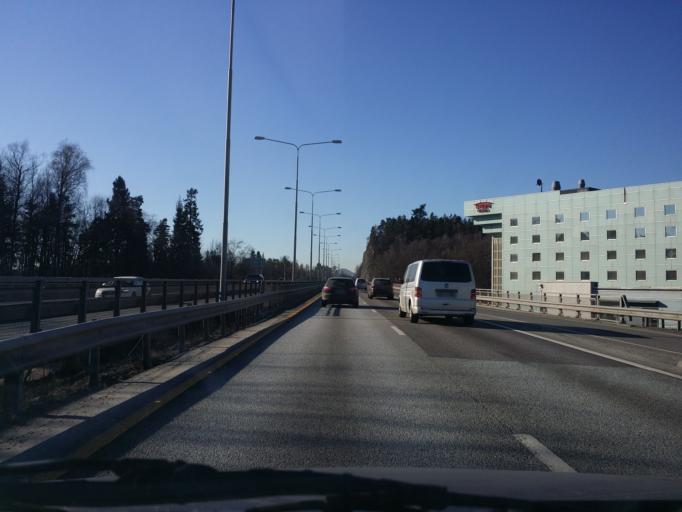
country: NO
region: Akershus
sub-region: Baerum
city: Sandvika
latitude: 59.8862
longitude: 10.5209
